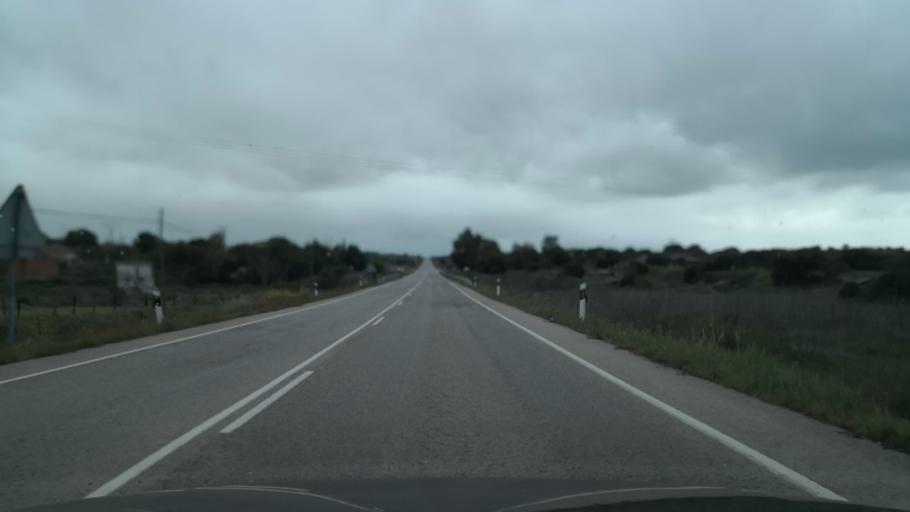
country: ES
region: Extremadura
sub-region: Provincia de Caceres
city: Malpartida de Caceres
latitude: 39.3897
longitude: -6.4331
